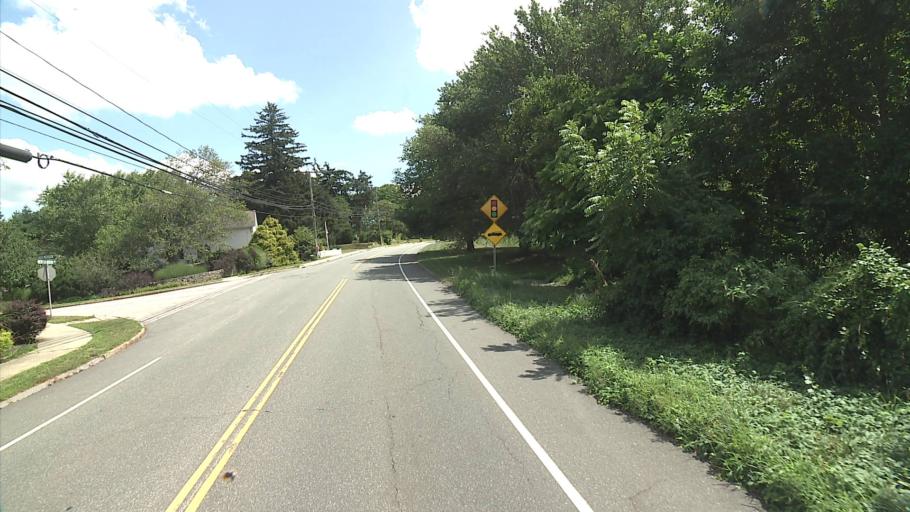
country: US
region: Connecticut
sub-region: New London County
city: Mystic
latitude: 41.3538
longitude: -71.9862
